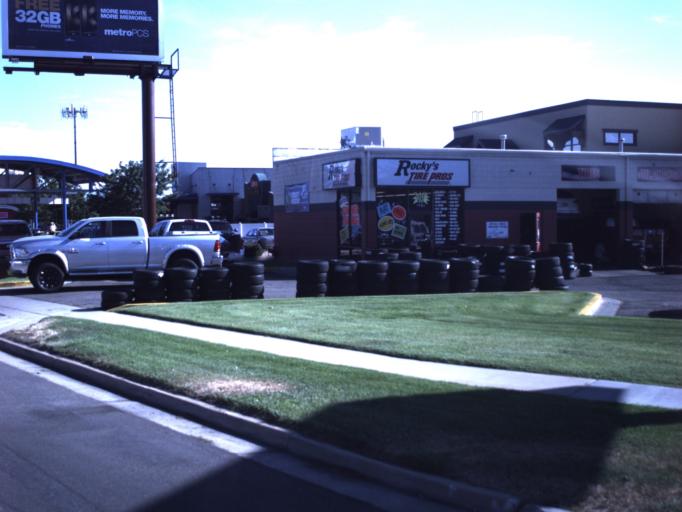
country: US
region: Utah
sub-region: Utah County
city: Orem
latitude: 40.3044
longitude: -111.6983
